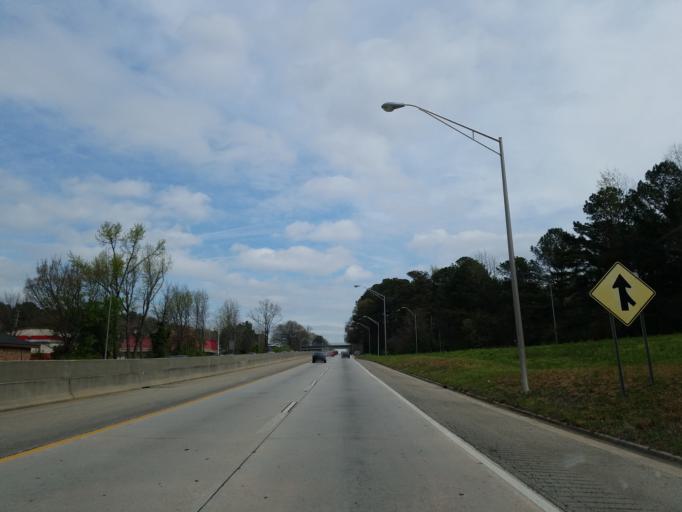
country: US
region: Georgia
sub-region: Fulton County
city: East Point
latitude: 33.6924
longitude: -84.4894
